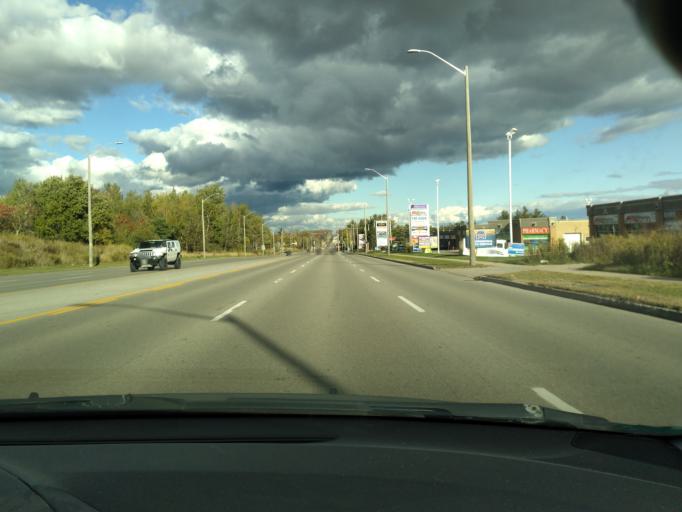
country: CA
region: Ontario
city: Innisfil
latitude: 44.3397
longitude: -79.6659
